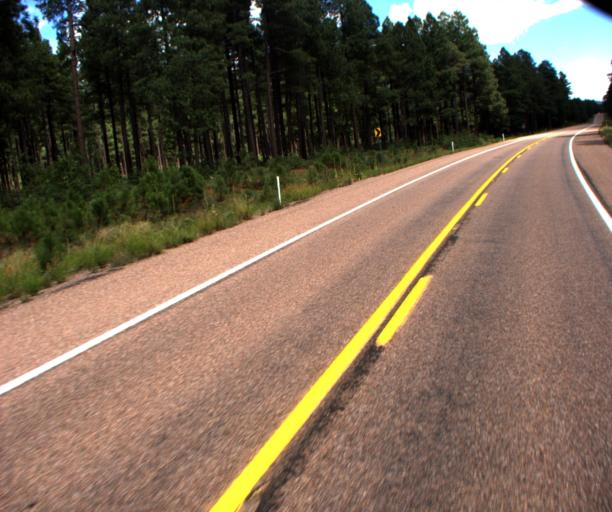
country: US
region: Arizona
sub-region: Navajo County
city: Pinetop-Lakeside
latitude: 34.0794
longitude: -109.8180
